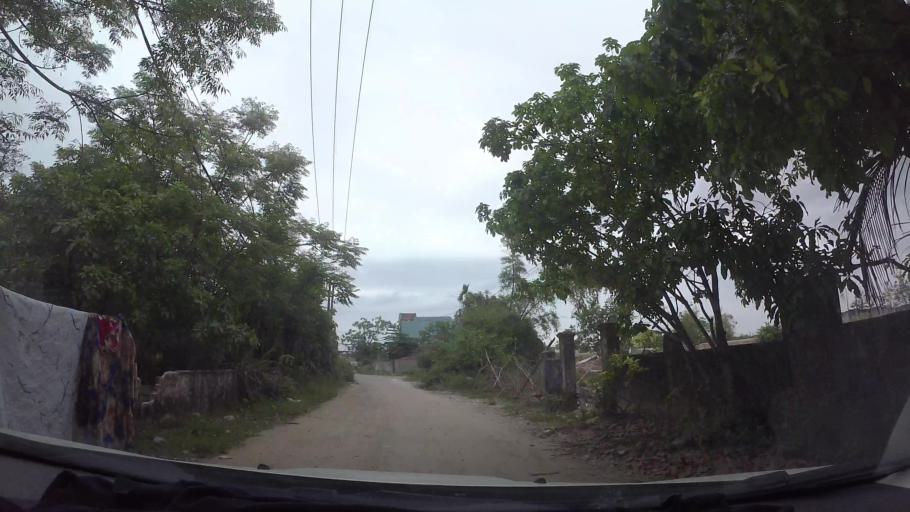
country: VN
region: Da Nang
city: Lien Chieu
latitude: 16.0900
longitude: 108.1061
